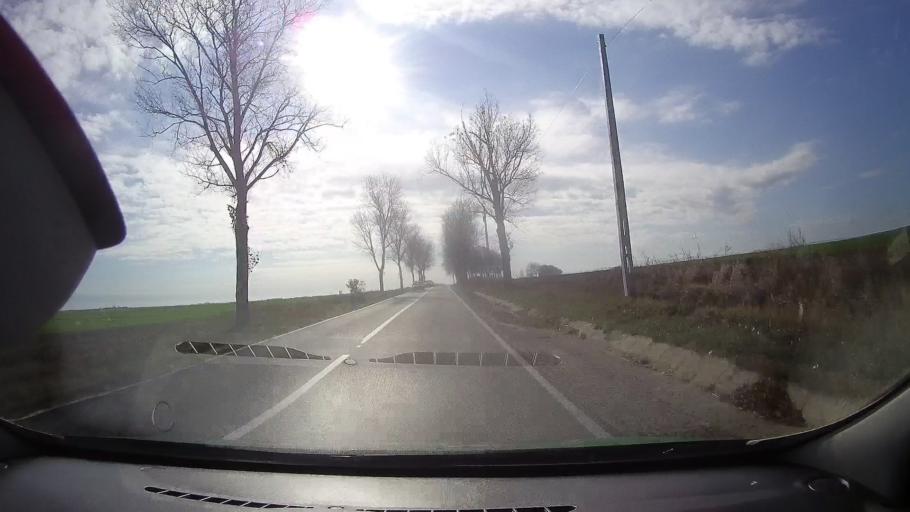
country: RO
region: Tulcea
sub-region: Comuna Valea Nucarilor
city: Agighiol
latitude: 44.9986
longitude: 28.8863
